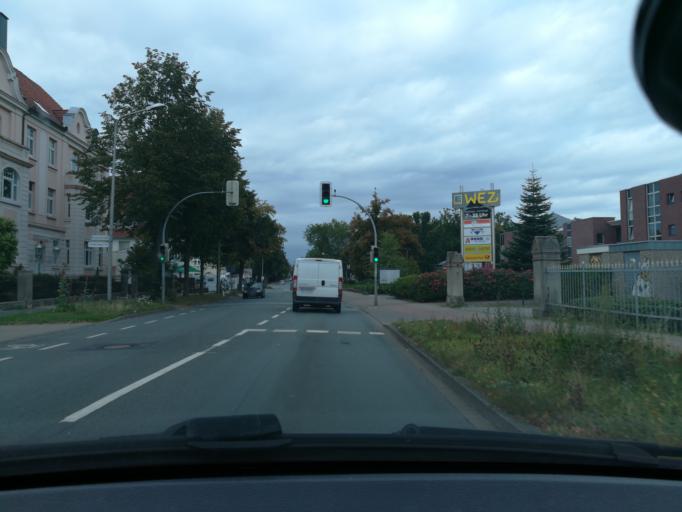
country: DE
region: North Rhine-Westphalia
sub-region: Regierungsbezirk Detmold
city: Minden
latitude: 52.3070
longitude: 8.9153
